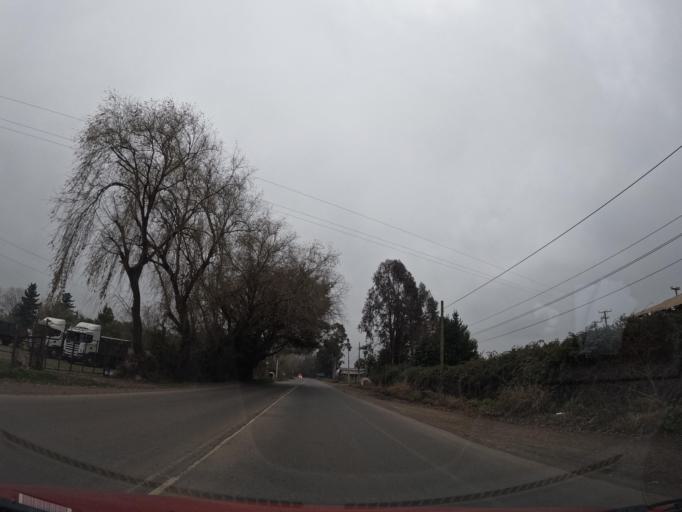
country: CL
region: Maule
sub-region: Provincia de Talca
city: San Clemente
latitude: -35.5527
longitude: -71.4693
